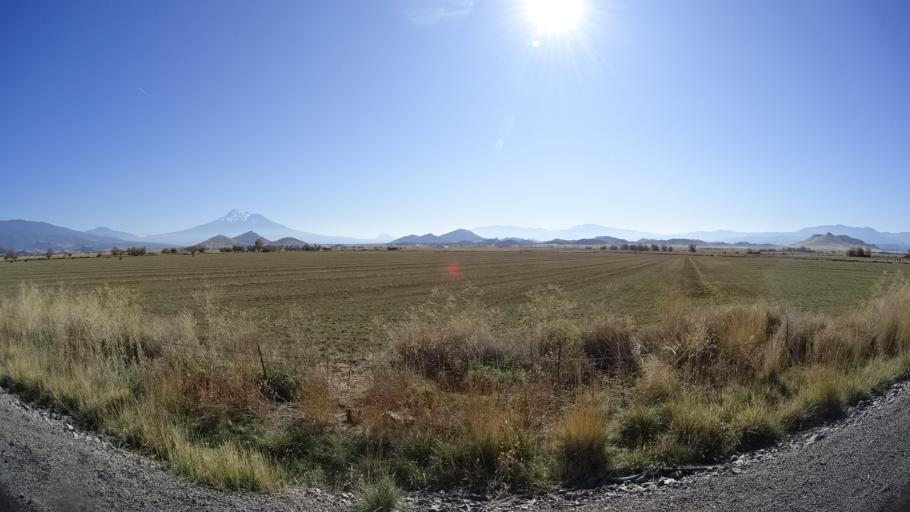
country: US
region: California
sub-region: Siskiyou County
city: Montague
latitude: 41.7263
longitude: -122.4240
